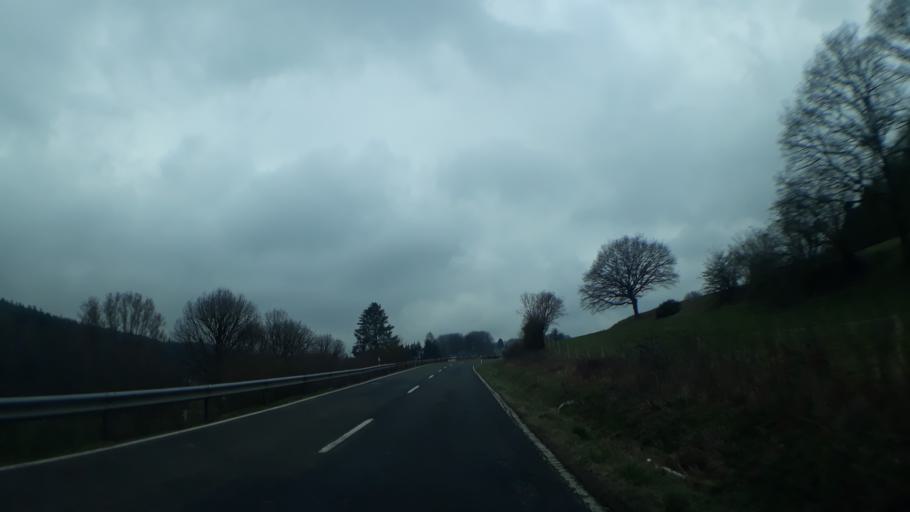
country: DE
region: North Rhine-Westphalia
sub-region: Regierungsbezirk Koln
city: Kall
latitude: 50.5310
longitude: 6.5378
